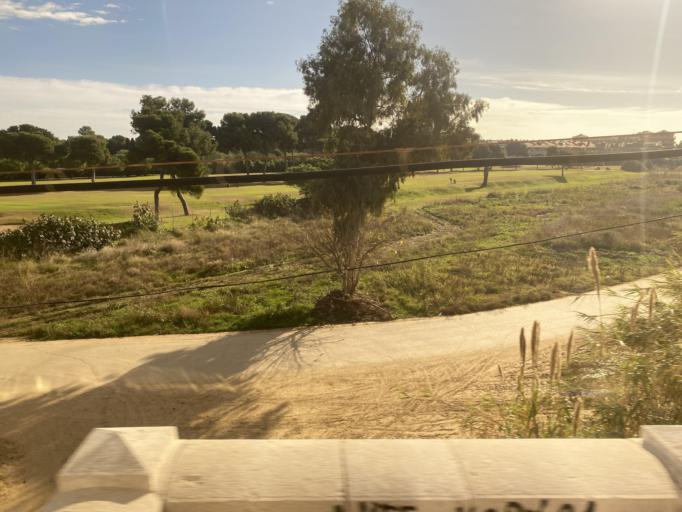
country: ES
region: Catalonia
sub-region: Provincia de Barcelona
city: Sitges
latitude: 41.2288
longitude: 1.7826
